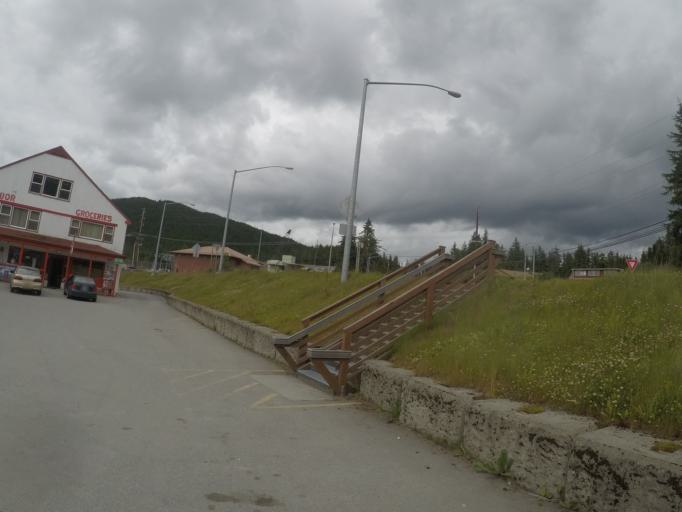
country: US
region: Alaska
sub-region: Juneau City and Borough
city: Juneau
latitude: 58.3860
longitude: -134.6444
